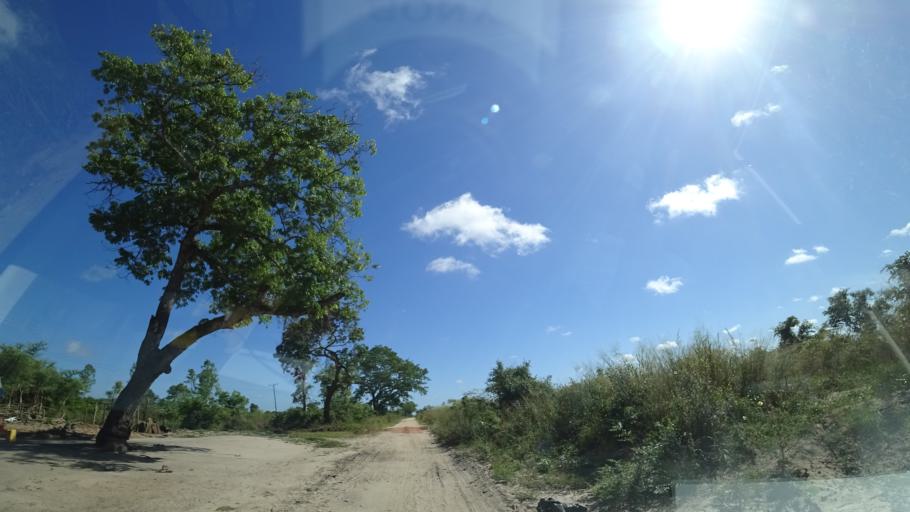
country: MZ
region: Sofala
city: Dondo
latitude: -19.2873
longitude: 34.6872
